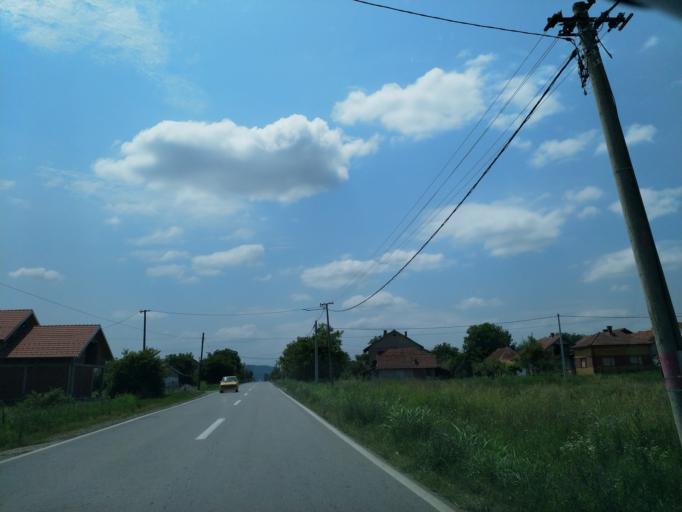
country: RS
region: Central Serbia
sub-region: Rasinski Okrug
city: Krusevac
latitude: 43.4659
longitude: 21.2513
